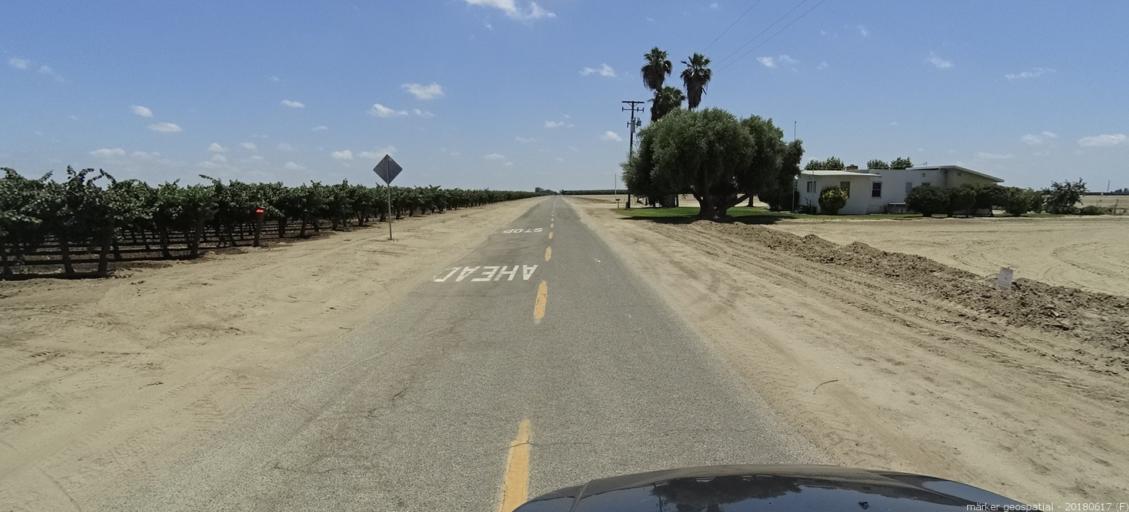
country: US
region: California
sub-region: Fresno County
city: Biola
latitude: 36.8352
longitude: -120.1330
